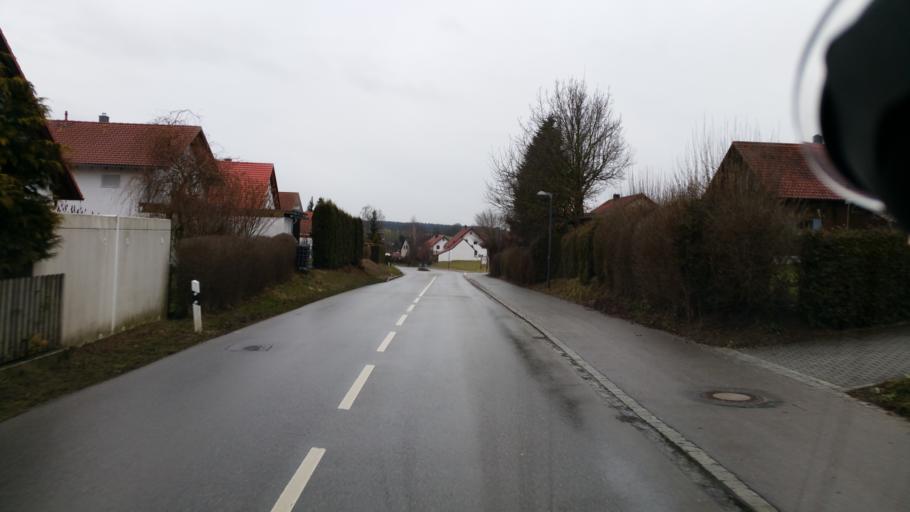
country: DE
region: Bavaria
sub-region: Lower Bavaria
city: Vilsheim
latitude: 48.4529
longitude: 12.1077
